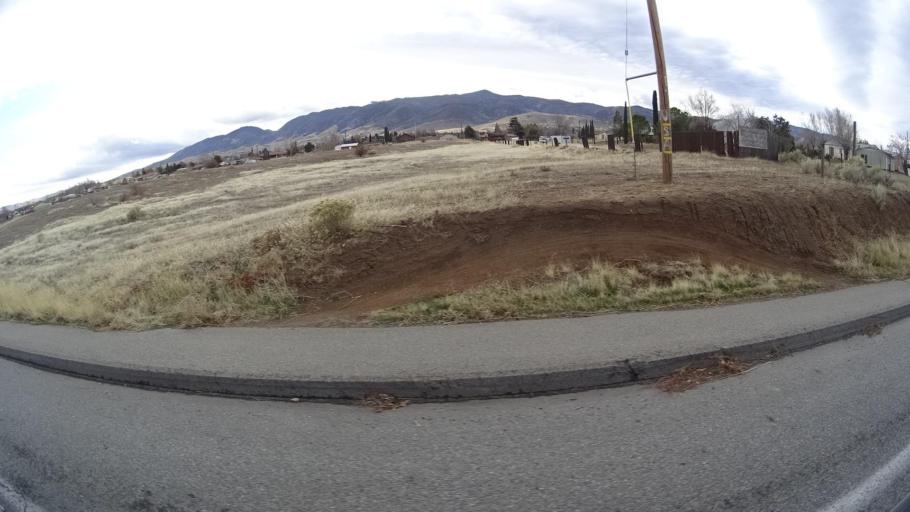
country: US
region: California
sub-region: Kern County
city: Golden Hills
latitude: 35.1315
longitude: -118.4740
